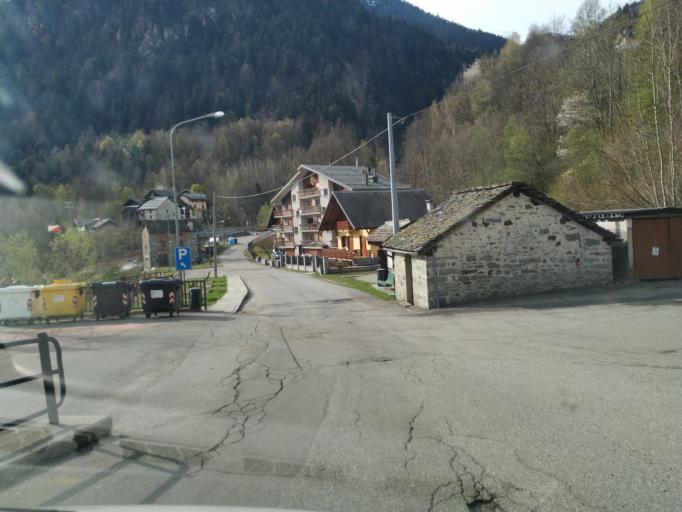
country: IT
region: Piedmont
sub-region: Provincia di Vercelli
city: Piode
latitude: 45.7702
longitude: 8.0499
